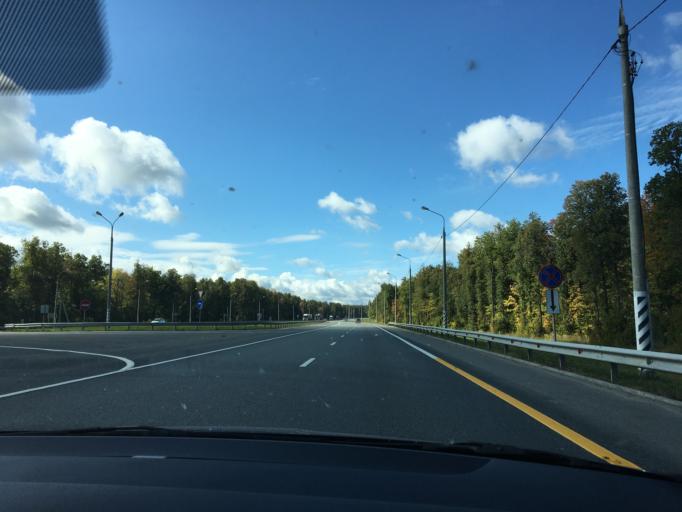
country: RU
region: Mariy-El
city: Vilovatovo
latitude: 56.0488
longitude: 46.4248
